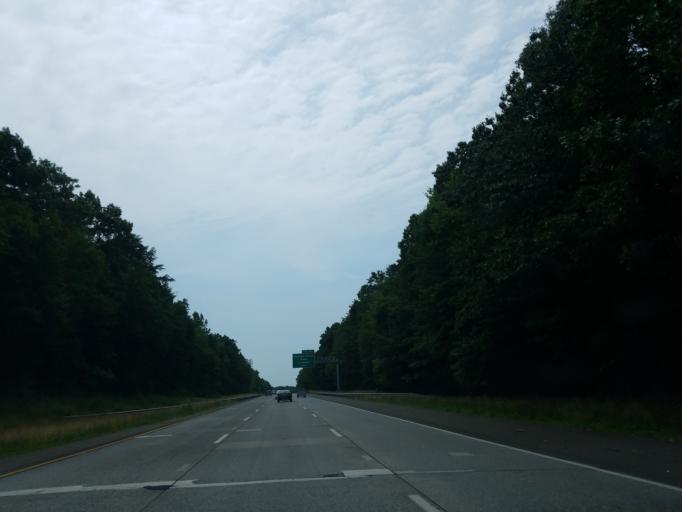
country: US
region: Connecticut
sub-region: Fairfield County
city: Trumbull
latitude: 41.2702
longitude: -73.2117
